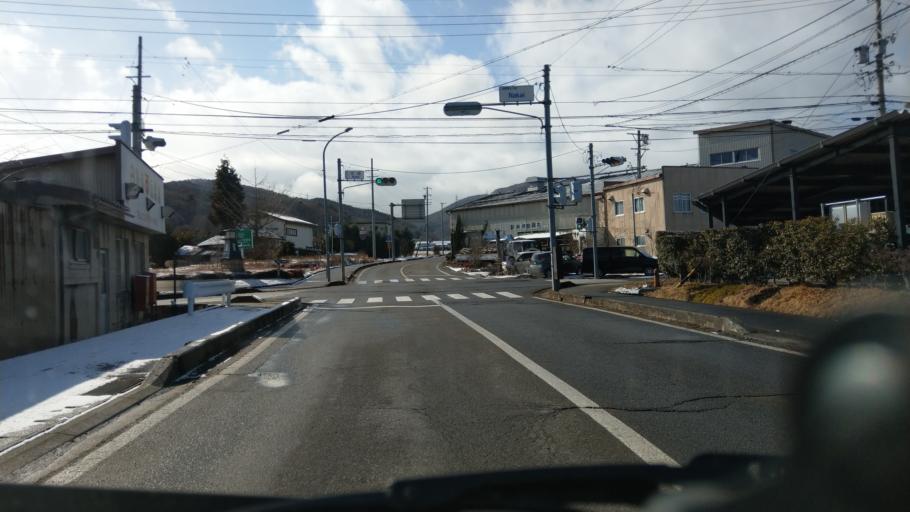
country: JP
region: Nagano
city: Kamimaruko
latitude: 36.2726
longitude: 138.3209
